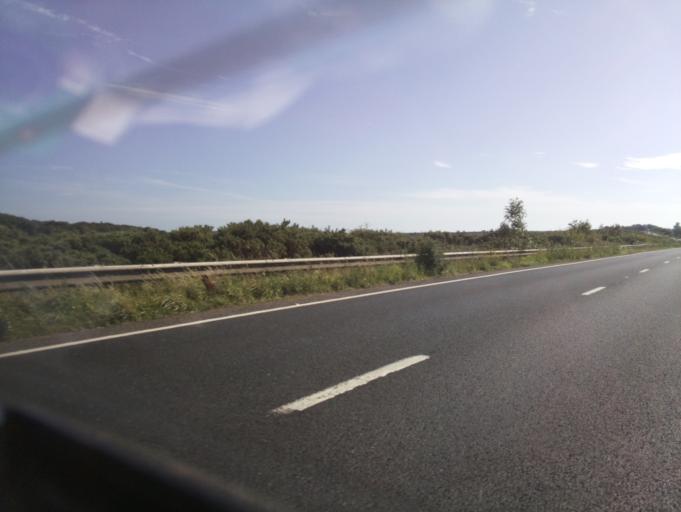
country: GB
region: England
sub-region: Hampshire
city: Ringwood
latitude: 50.8625
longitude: -1.7163
